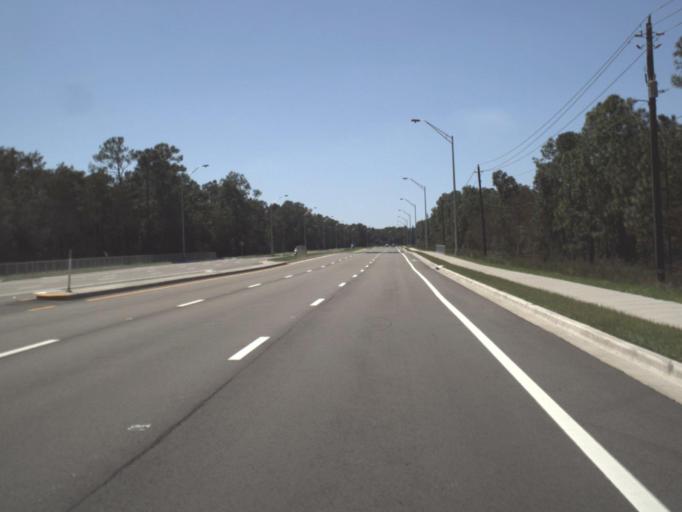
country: US
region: Florida
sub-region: Collier County
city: Golden Gate
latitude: 26.1479
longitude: -81.7022
